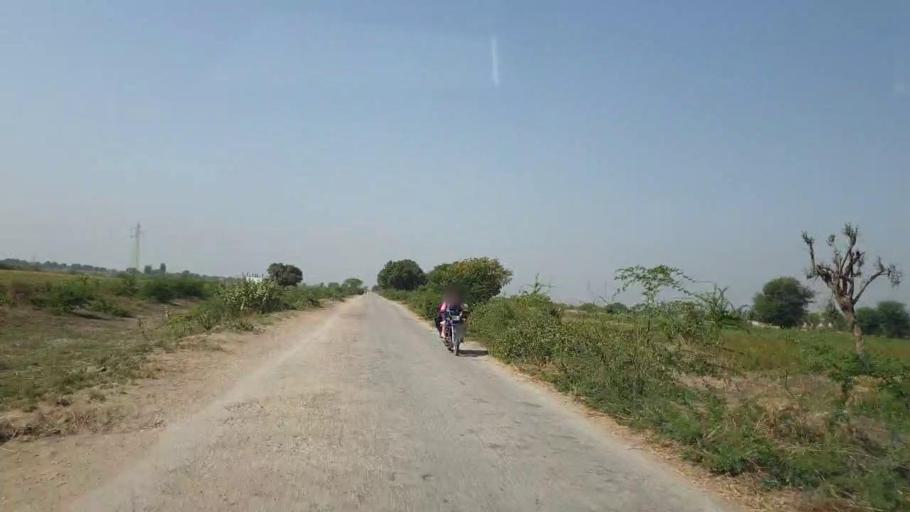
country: PK
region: Sindh
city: Naukot
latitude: 25.0189
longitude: 69.4724
